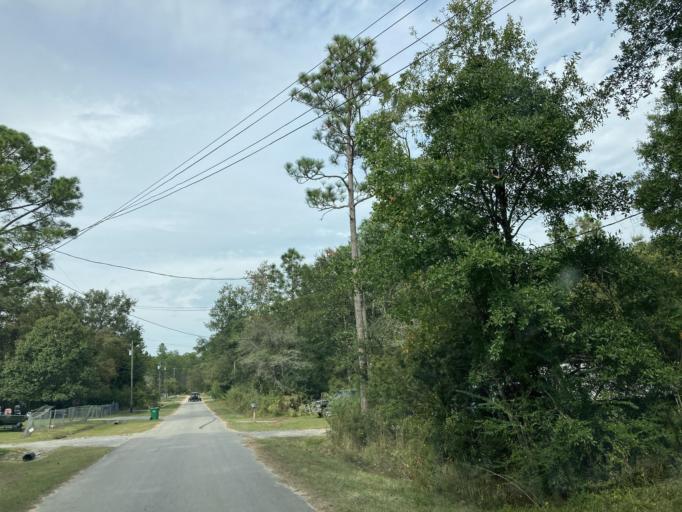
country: US
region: Mississippi
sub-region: Jackson County
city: Saint Martin
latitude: 30.4777
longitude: -88.8463
